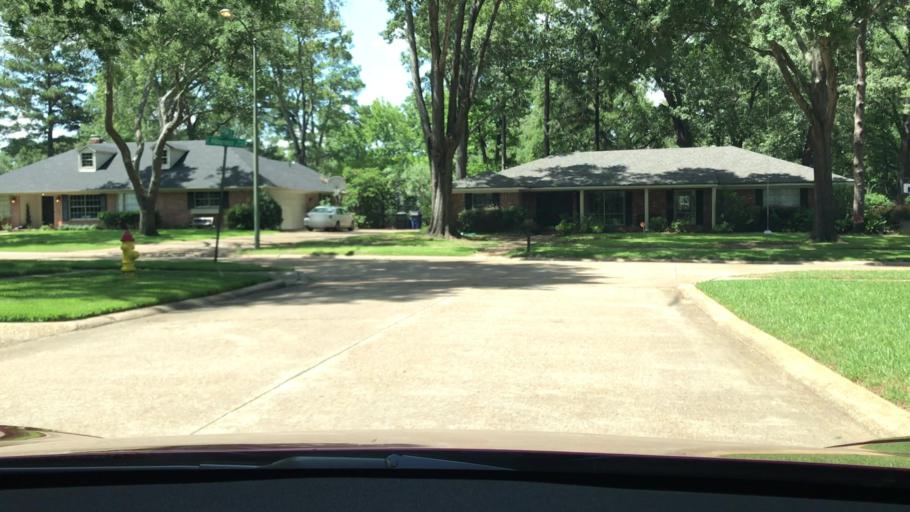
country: US
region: Louisiana
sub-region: Bossier Parish
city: Bossier City
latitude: 32.4306
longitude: -93.7351
